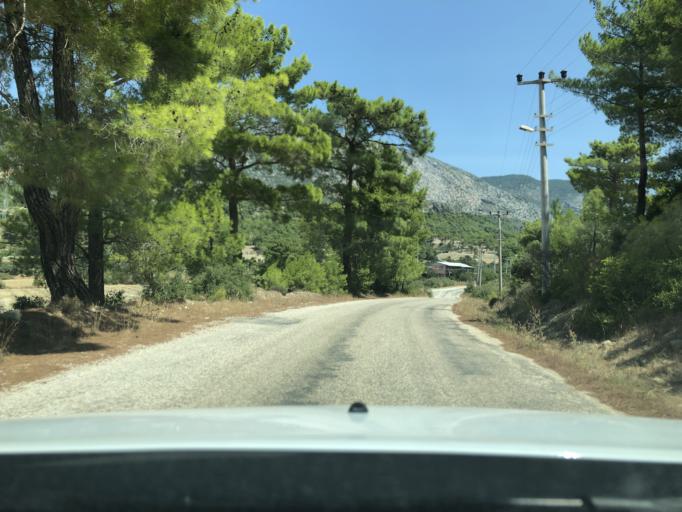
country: TR
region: Antalya
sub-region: Manavgat
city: Kizilagac
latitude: 36.8568
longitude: 31.5604
